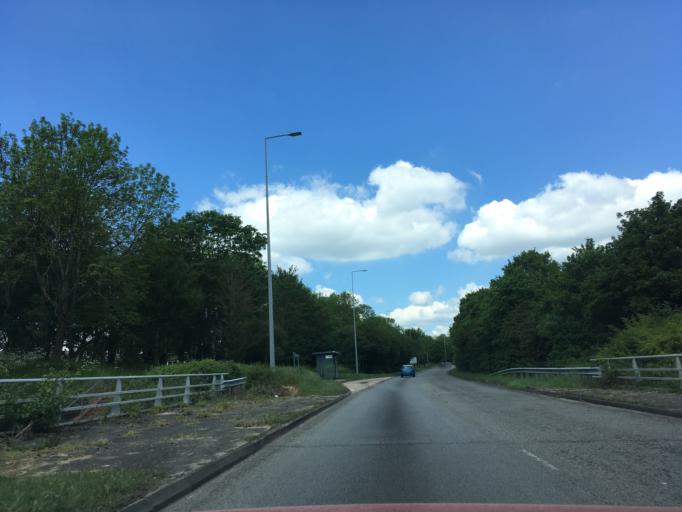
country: GB
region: England
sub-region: Milton Keynes
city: Milton Keynes
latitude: 52.0289
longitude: -0.7339
